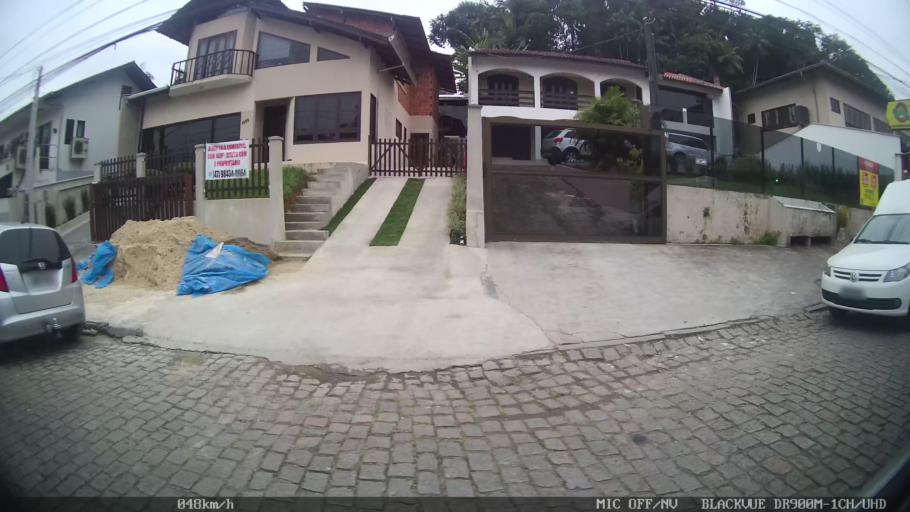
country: BR
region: Santa Catarina
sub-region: Joinville
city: Joinville
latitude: -26.3380
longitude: -48.8574
